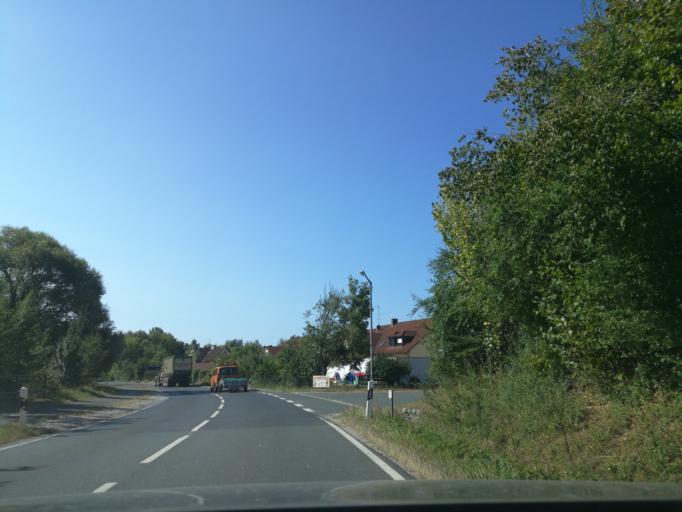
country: DE
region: Bavaria
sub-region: Regierungsbezirk Mittelfranken
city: Ammerndorf
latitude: 49.4256
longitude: 10.8530
